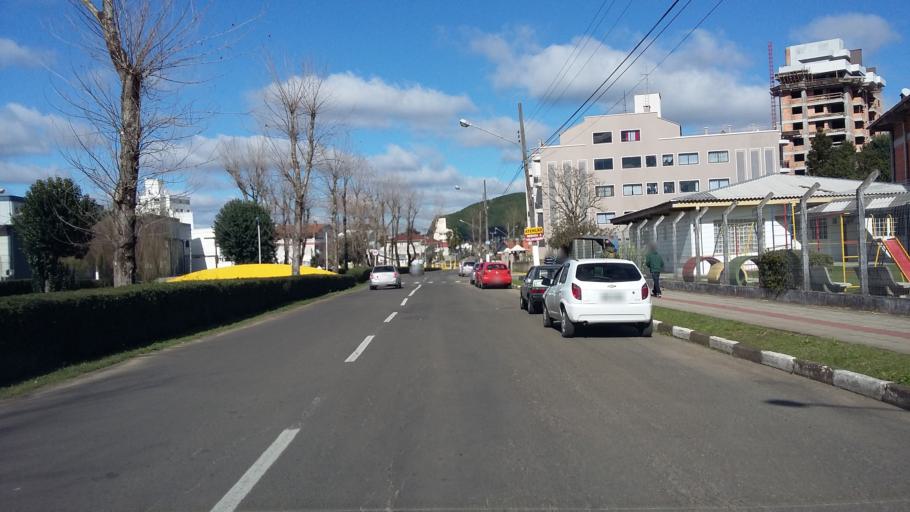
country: BR
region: Santa Catarina
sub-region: Lages
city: Lages
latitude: -27.8169
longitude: -50.3187
